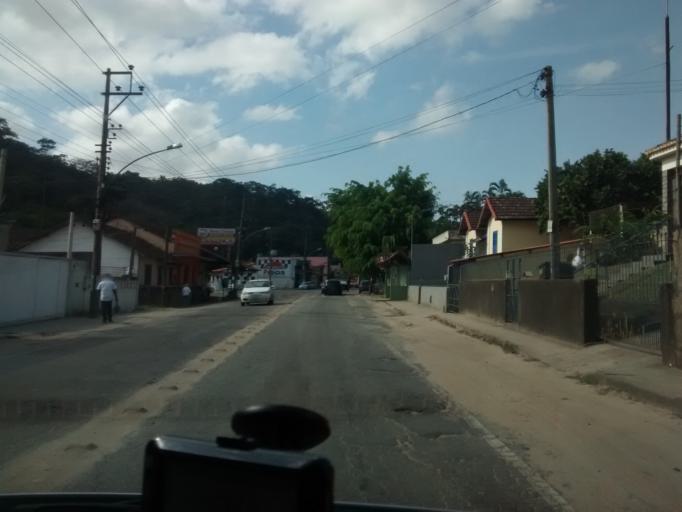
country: BR
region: Rio de Janeiro
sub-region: Miguel Pereira
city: Miguel Pereira
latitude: -22.4603
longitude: -43.4810
